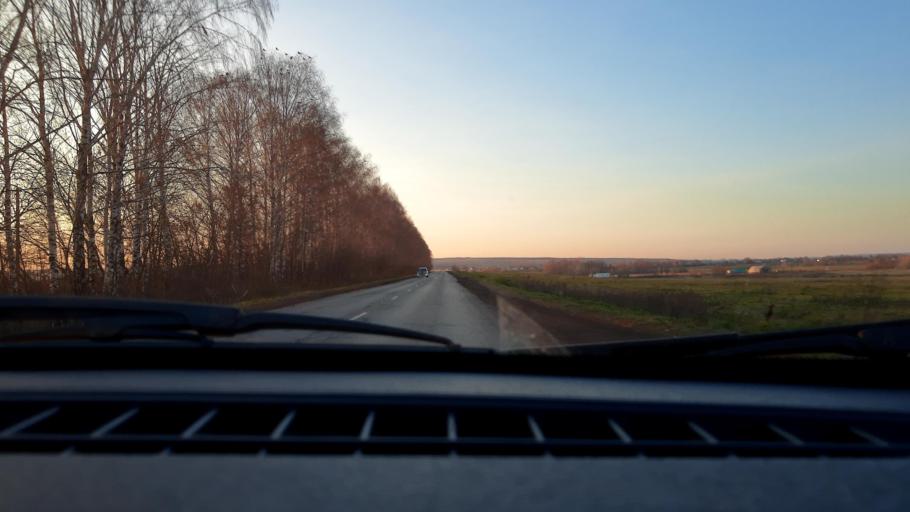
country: RU
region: Bashkortostan
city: Ufa
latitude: 54.8260
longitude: 55.9795
